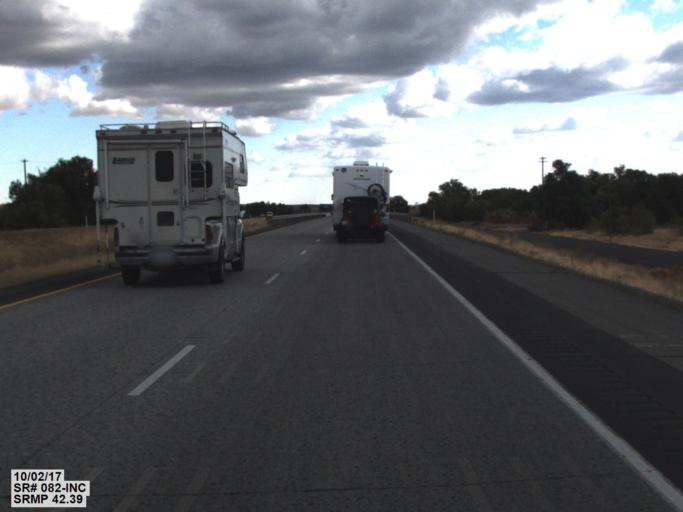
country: US
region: Washington
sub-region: Yakima County
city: Wapato
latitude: 46.4902
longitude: -120.4251
